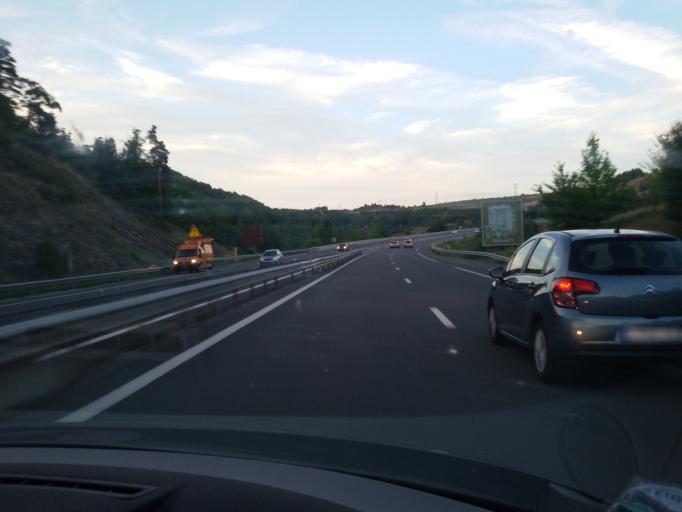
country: FR
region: Languedoc-Roussillon
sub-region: Departement de la Lozere
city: Chirac
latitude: 44.5346
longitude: 3.2519
